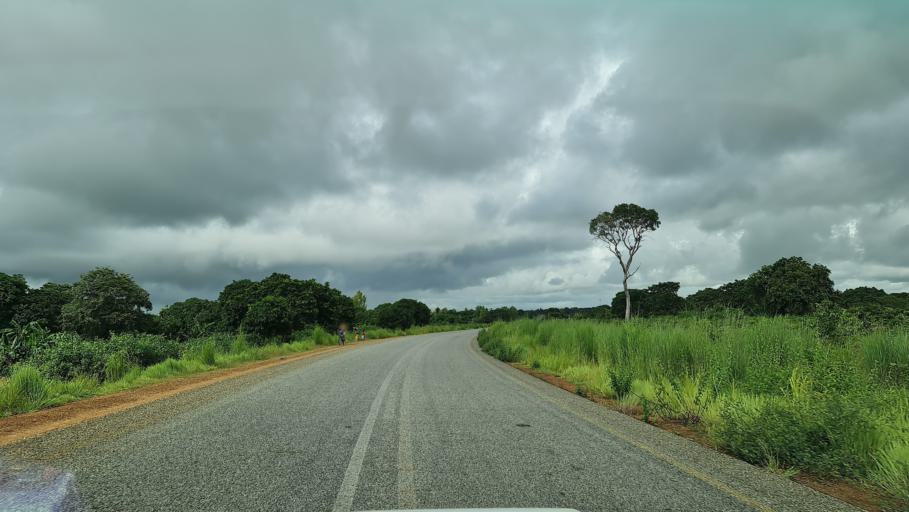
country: MZ
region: Nampula
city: Nampula
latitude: -15.0529
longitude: 38.4205
